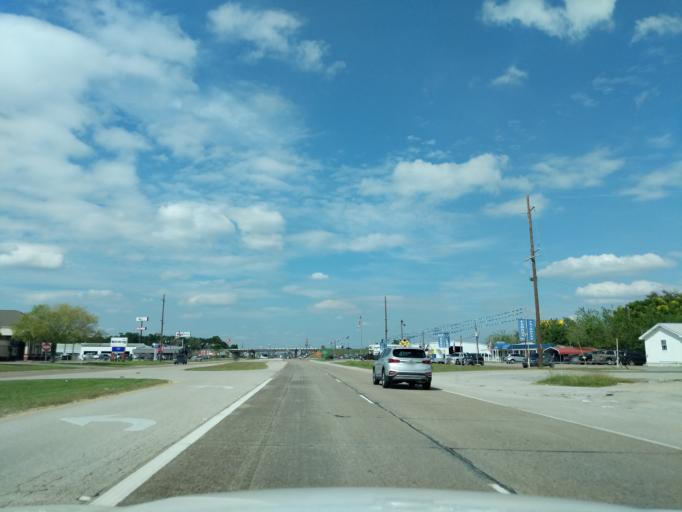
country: US
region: Texas
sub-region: Chambers County
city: Winnie
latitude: 29.8233
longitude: -94.3839
